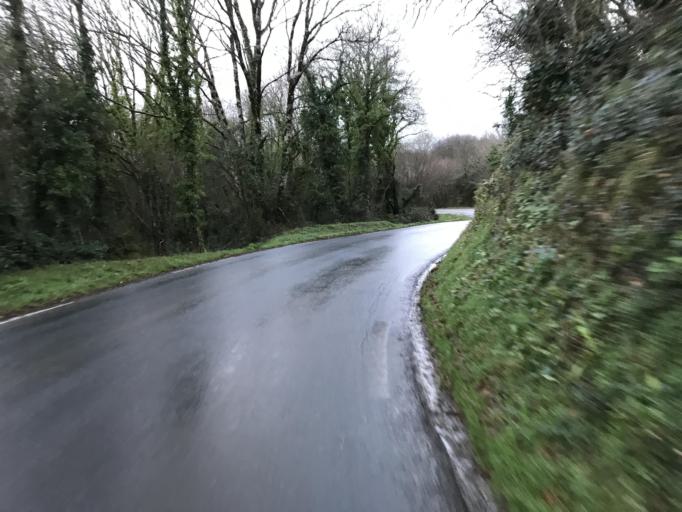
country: FR
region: Brittany
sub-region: Departement du Finistere
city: Plougastel-Daoulas
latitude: 48.3607
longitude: -4.3582
